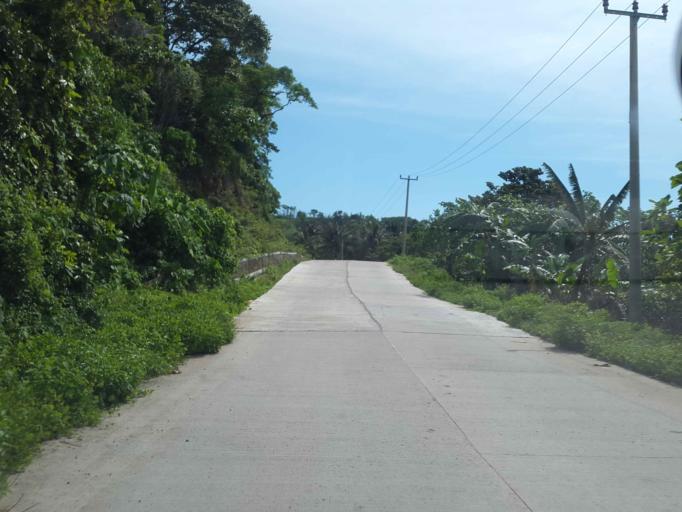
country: ID
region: Banten
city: Babakanbungur
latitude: -6.5148
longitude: 105.6347
